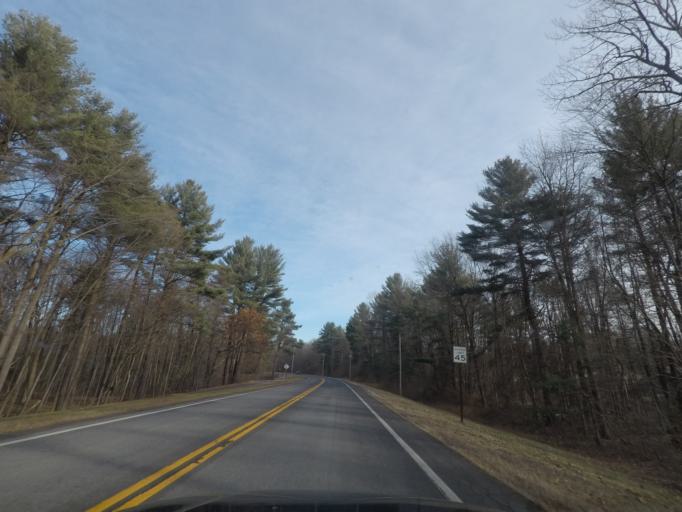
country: US
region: New York
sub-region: Saratoga County
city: Country Knolls
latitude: 42.9767
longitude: -73.7710
